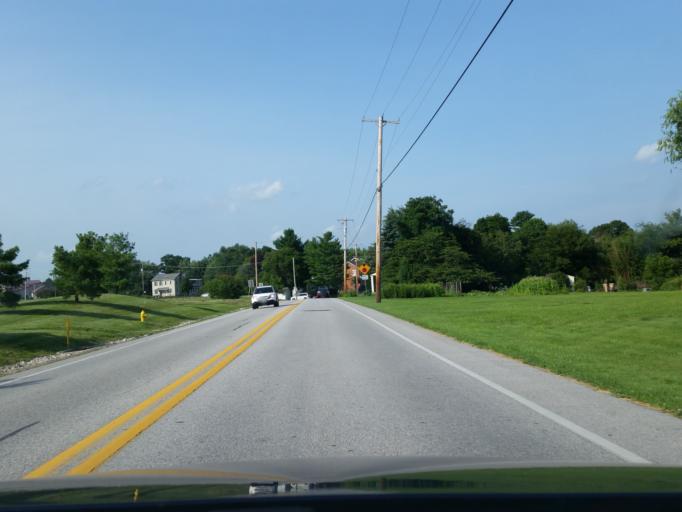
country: US
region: Pennsylvania
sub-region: York County
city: Emigsville
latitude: 40.0089
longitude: -76.7587
